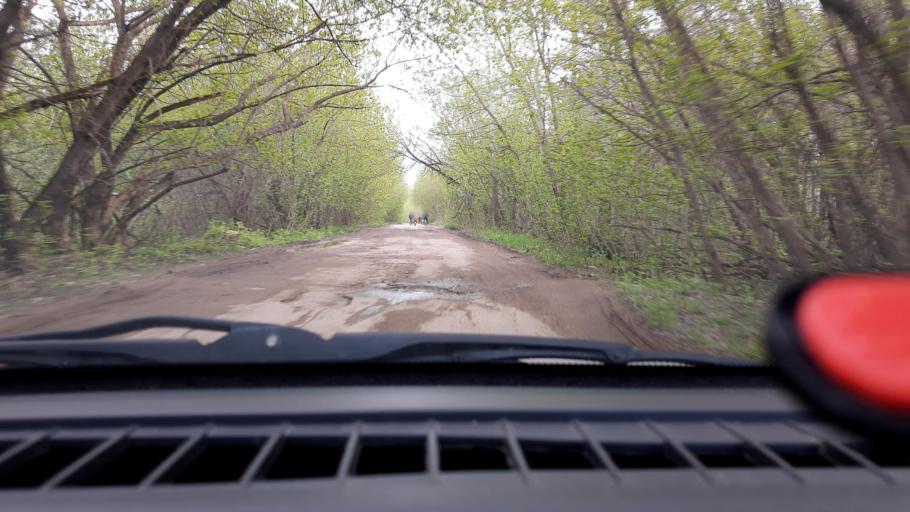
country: RU
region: Nizjnij Novgorod
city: Neklyudovo
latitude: 56.3885
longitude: 43.8418
